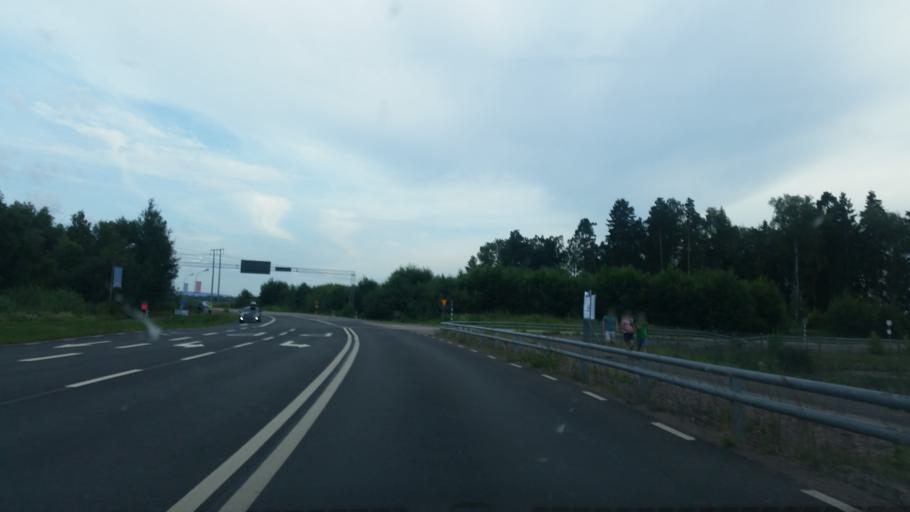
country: SE
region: Vaestra Goetaland
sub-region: Skara Kommun
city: Axvall
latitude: 58.4023
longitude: 13.5511
